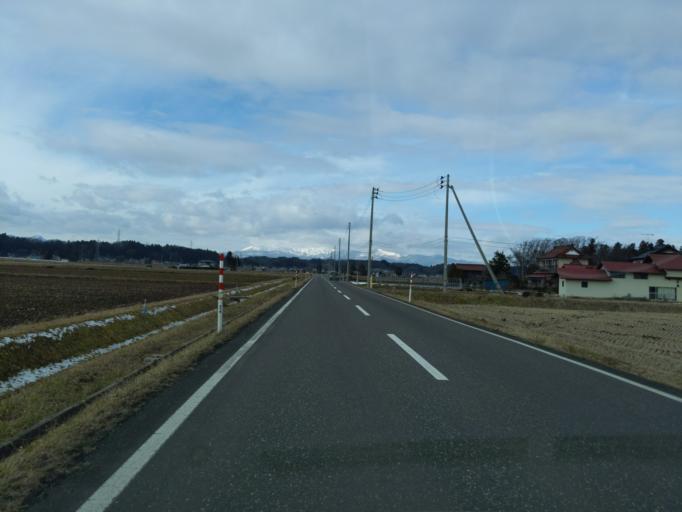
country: JP
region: Iwate
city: Mizusawa
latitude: 39.0894
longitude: 141.1509
